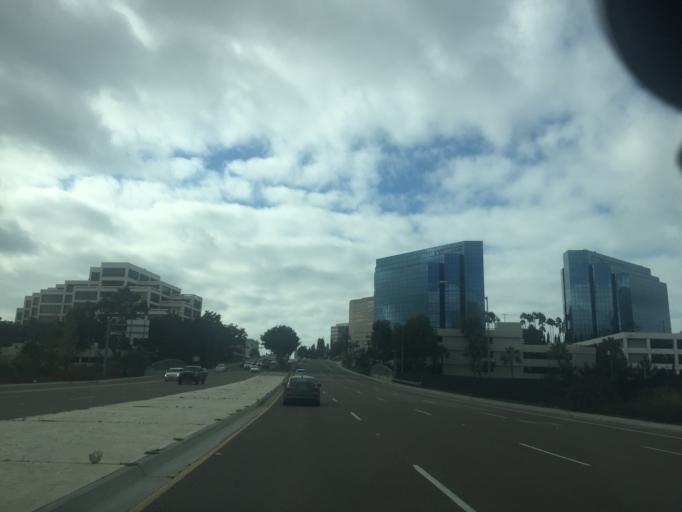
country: US
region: California
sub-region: San Diego County
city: La Jolla
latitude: 32.8745
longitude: -117.2042
